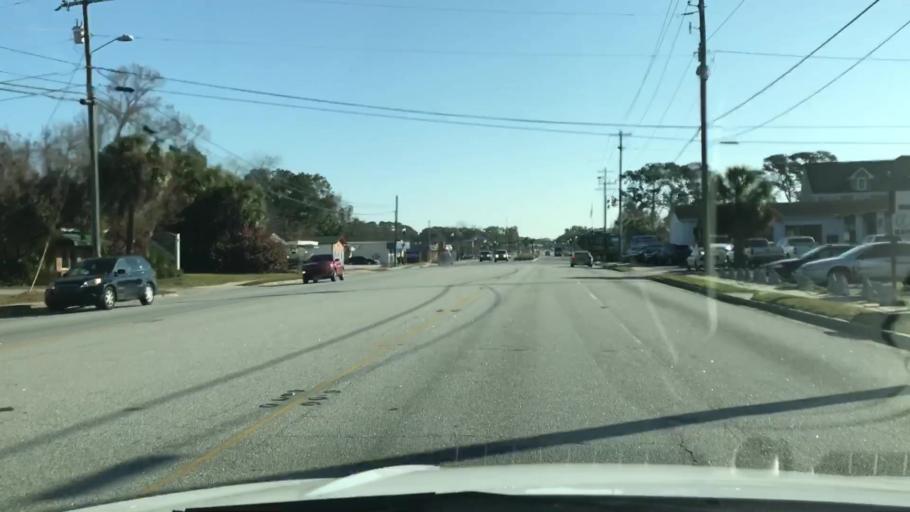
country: US
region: South Carolina
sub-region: Beaufort County
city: Burton
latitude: 32.4400
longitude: -80.7088
